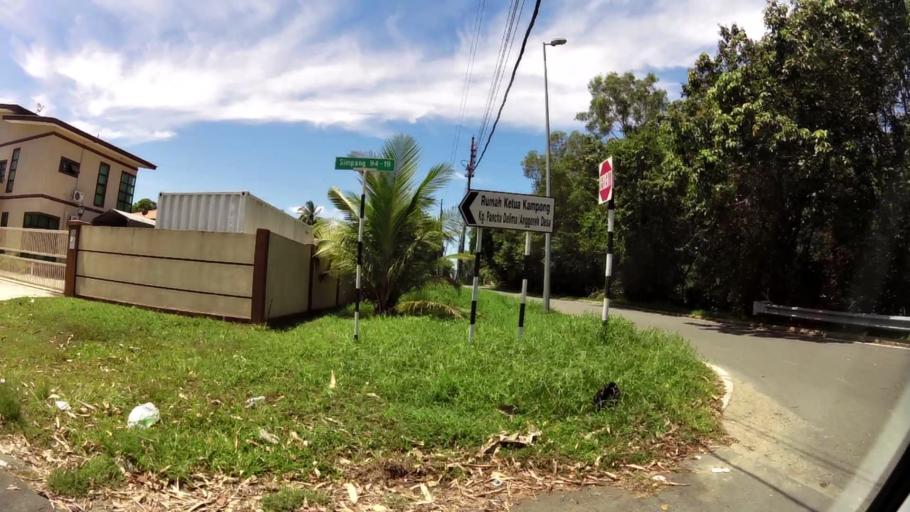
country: BN
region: Brunei and Muara
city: Bandar Seri Begawan
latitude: 4.9429
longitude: 114.9491
